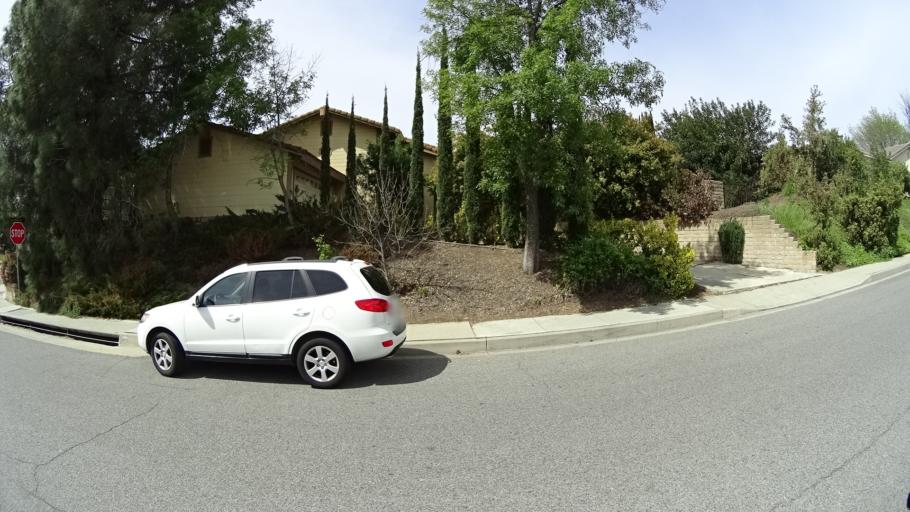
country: US
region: California
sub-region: Ventura County
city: Thousand Oaks
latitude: 34.1479
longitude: -118.8489
